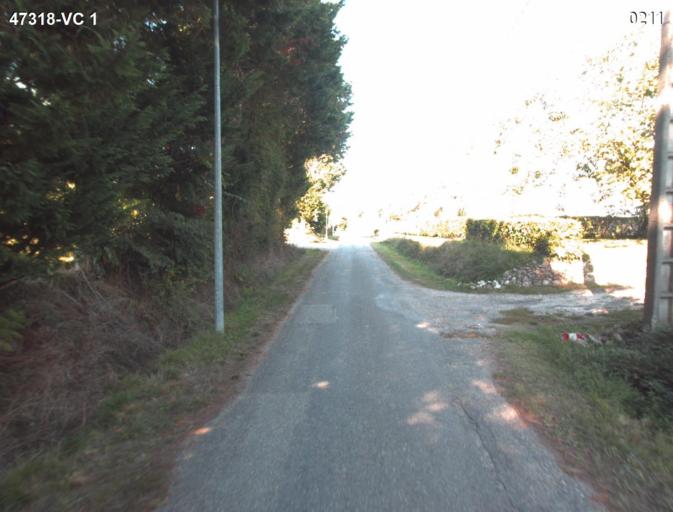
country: FR
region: Aquitaine
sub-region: Departement du Lot-et-Garonne
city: Vianne
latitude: 44.2267
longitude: 0.3227
